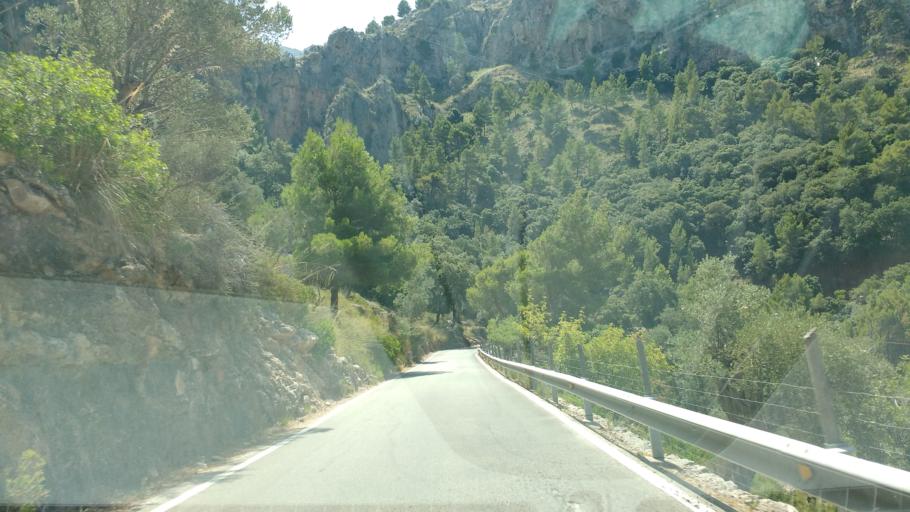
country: ES
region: Balearic Islands
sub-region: Illes Balears
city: Escorca
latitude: 39.8397
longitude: 2.7991
